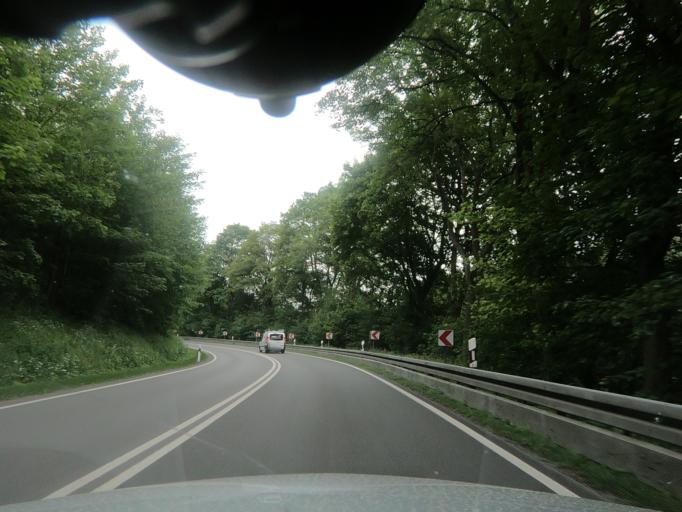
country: DE
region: North Rhine-Westphalia
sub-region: Regierungsbezirk Arnsberg
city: Olsberg
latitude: 51.3243
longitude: 8.4952
